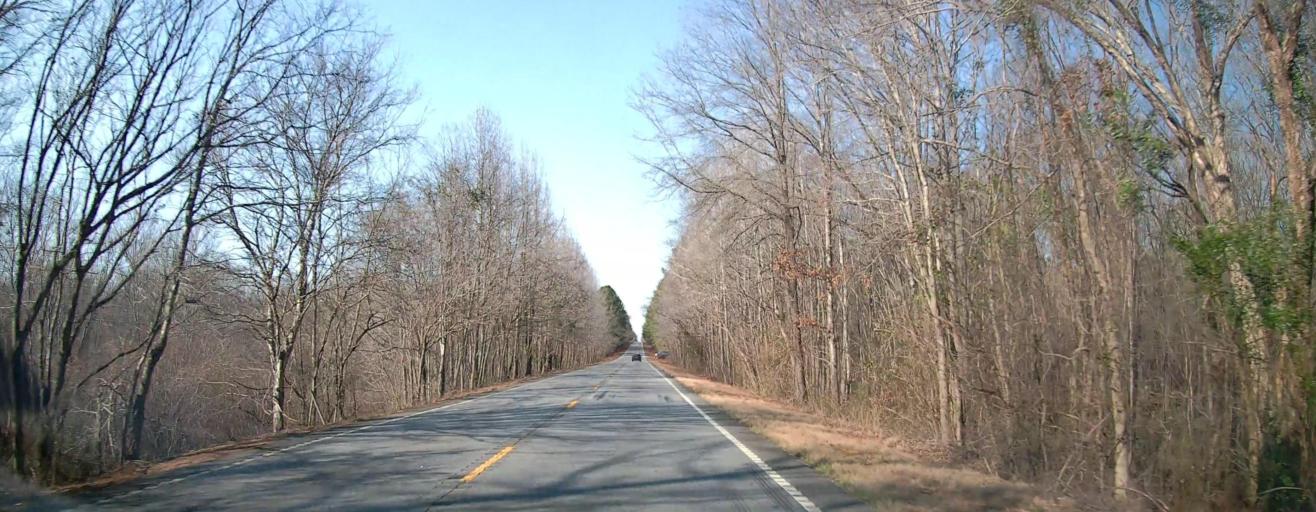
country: US
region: Georgia
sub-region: Butts County
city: Indian Springs
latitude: 33.1660
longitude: -83.8422
